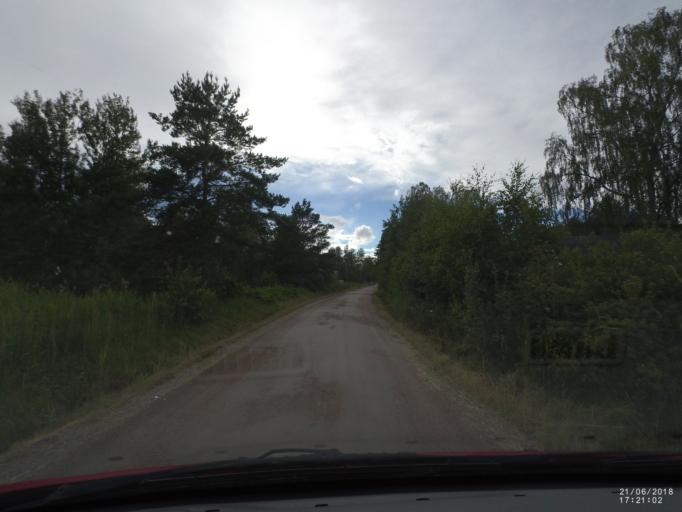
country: SE
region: Soedermanland
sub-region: Nykopings Kommun
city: Nykoping
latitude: 58.7510
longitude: 17.0694
